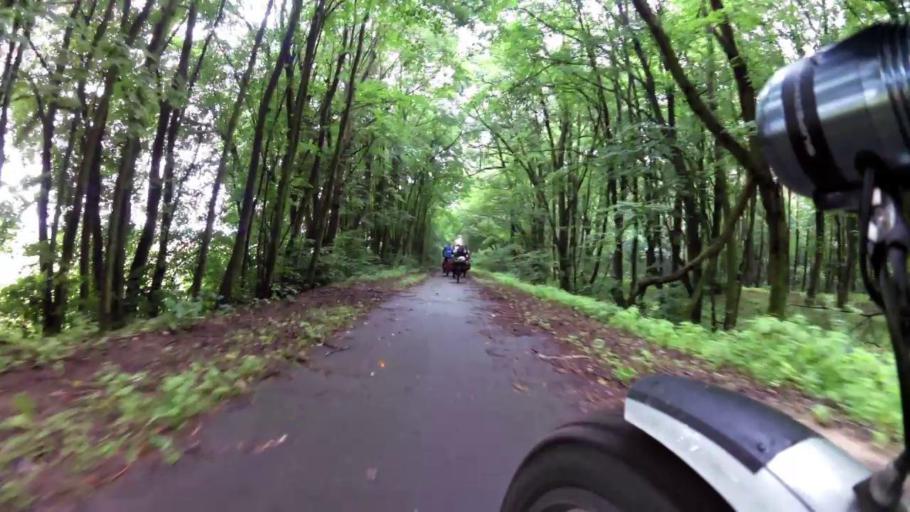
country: PL
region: West Pomeranian Voivodeship
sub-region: Powiat gryfinski
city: Banie
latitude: 53.0694
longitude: 14.6290
